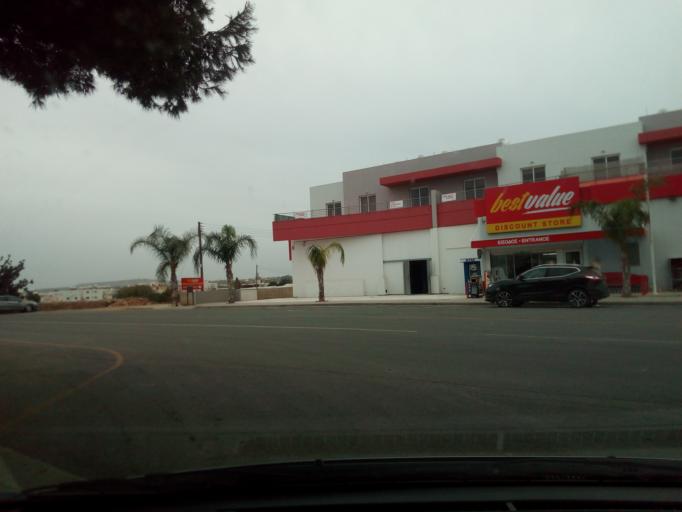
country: CY
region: Ammochostos
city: Paralimni
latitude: 35.0511
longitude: 34.0136
